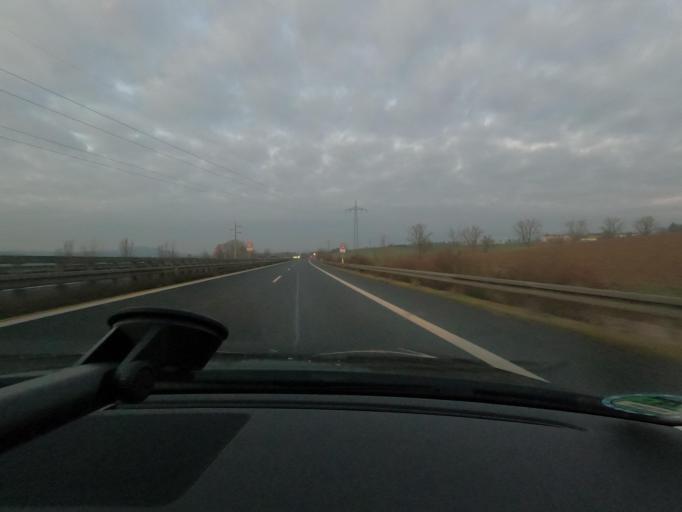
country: DE
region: Bavaria
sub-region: Upper Franconia
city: Ebensfeld
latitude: 50.0471
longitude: 10.9594
